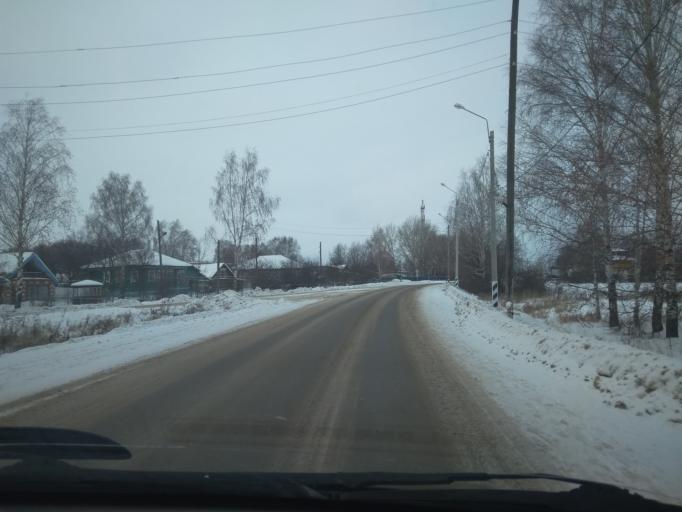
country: RU
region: Mordoviya
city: Ten'gushevo
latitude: 54.7572
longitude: 42.7104
